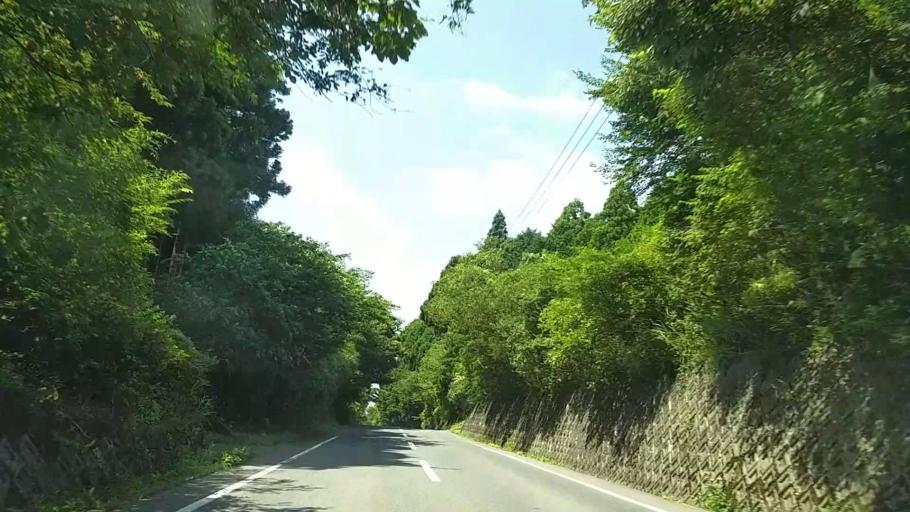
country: JP
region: Shizuoka
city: Fuji
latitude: 35.2490
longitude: 138.7068
